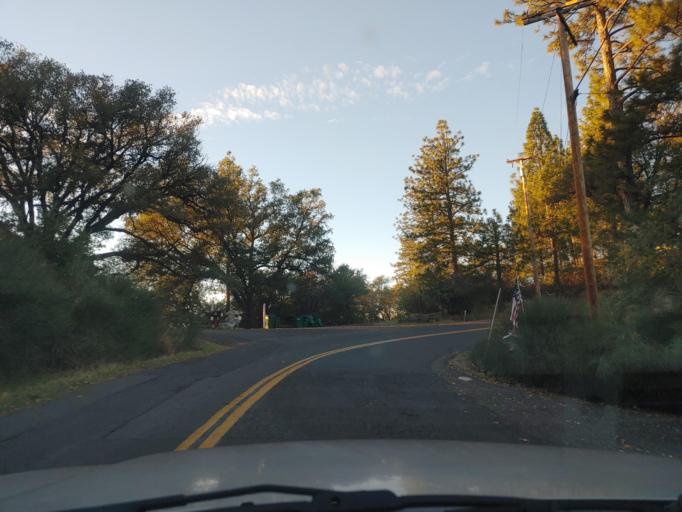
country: US
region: California
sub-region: Tuolumne County
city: Columbia
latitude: 38.0382
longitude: -120.3690
